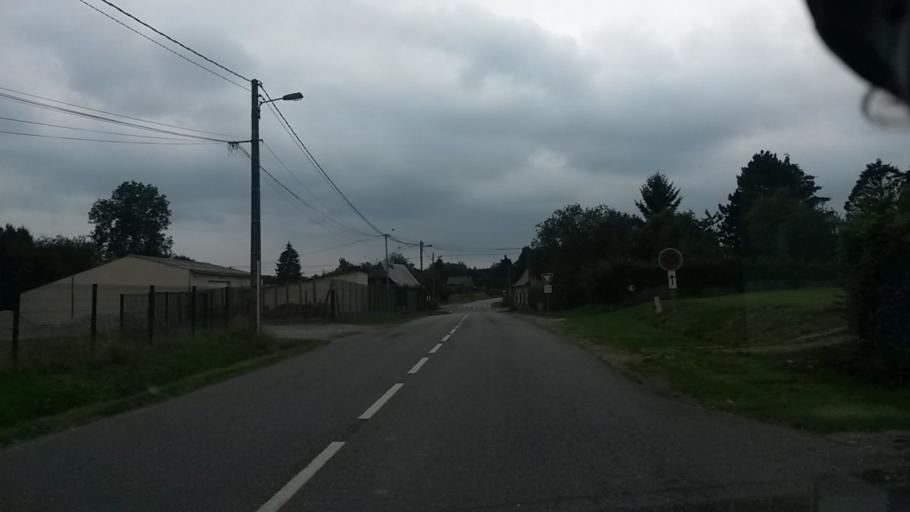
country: FR
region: Haute-Normandie
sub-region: Departement de la Seine-Maritime
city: Gaillefontaine
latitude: 49.6920
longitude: 1.6390
